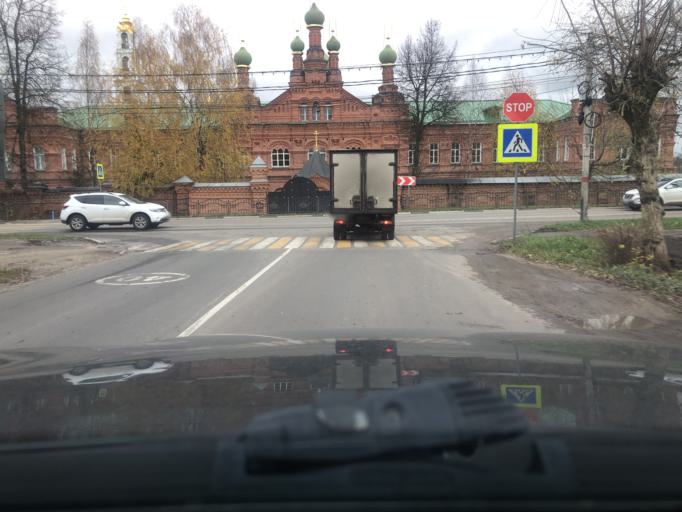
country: RU
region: Moskovskaya
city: Sergiyev Posad
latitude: 56.3092
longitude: 38.1250
